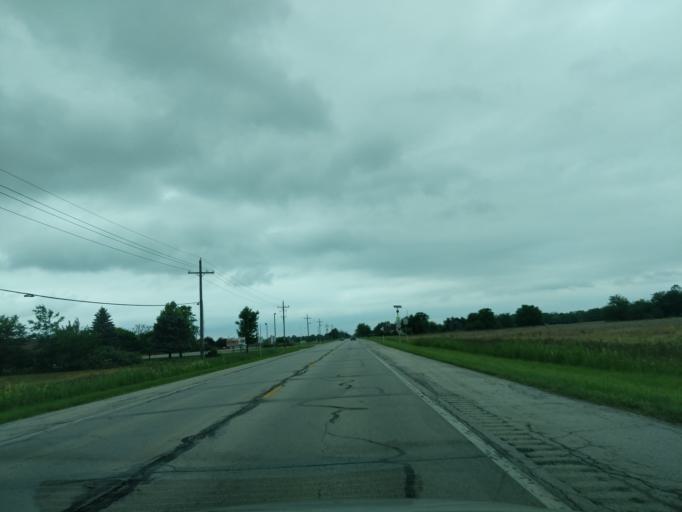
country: US
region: Indiana
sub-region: Hamilton County
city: Arcadia
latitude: 40.1532
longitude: -86.0133
